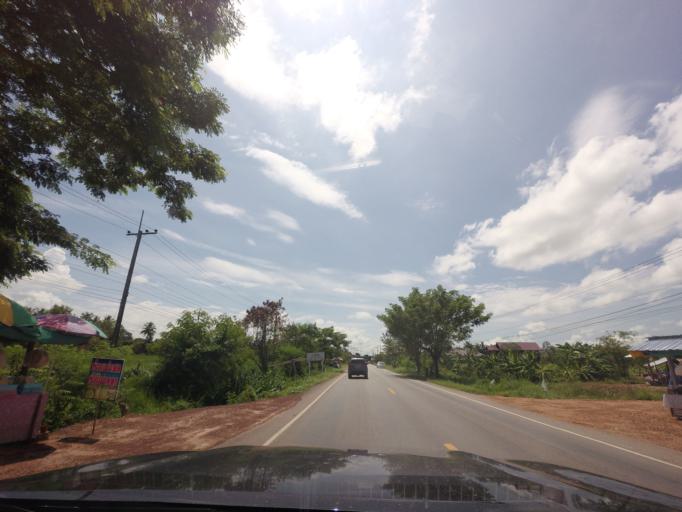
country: TH
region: Changwat Udon Thani
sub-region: Amphoe Ban Phue
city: Ban Phue
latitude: 17.7518
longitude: 102.3987
